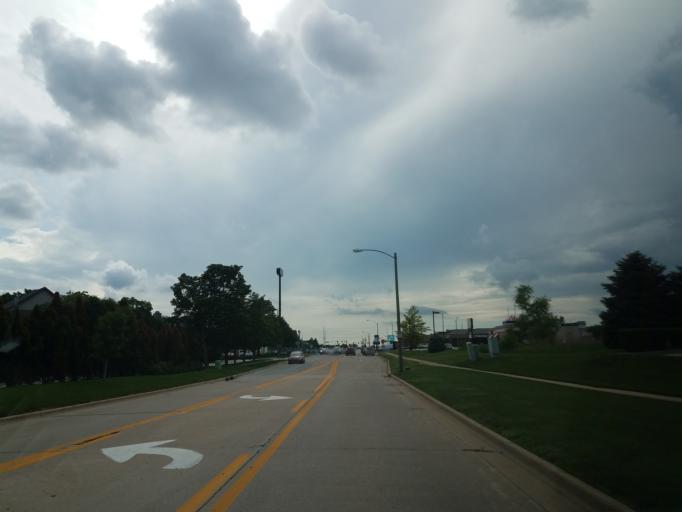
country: US
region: Illinois
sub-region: McLean County
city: Bloomington
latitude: 40.4841
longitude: -88.9479
